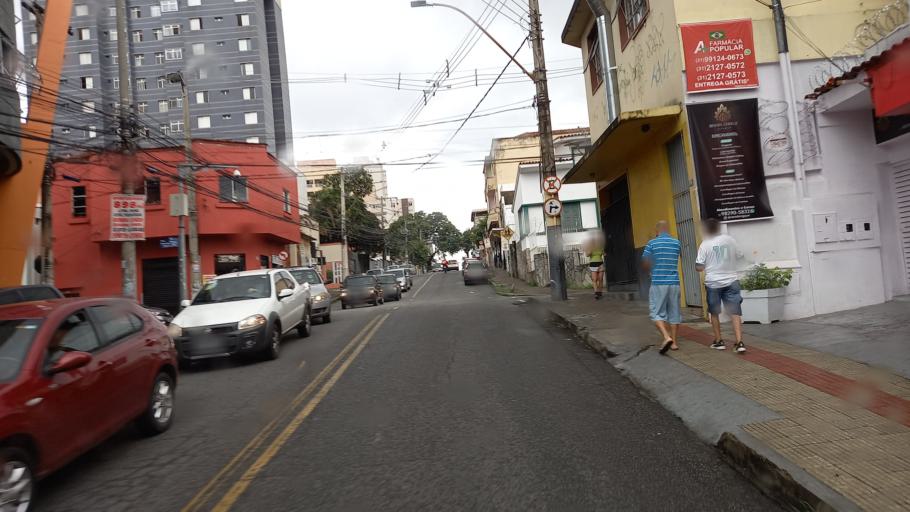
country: BR
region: Minas Gerais
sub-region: Belo Horizonte
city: Belo Horizonte
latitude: -19.9171
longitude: -43.9257
